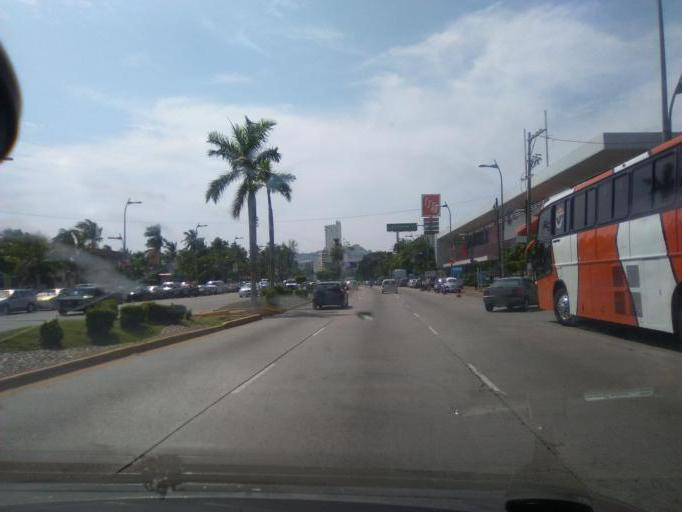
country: MX
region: Guerrero
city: Acapulco de Juarez
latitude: 16.8580
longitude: -99.8894
